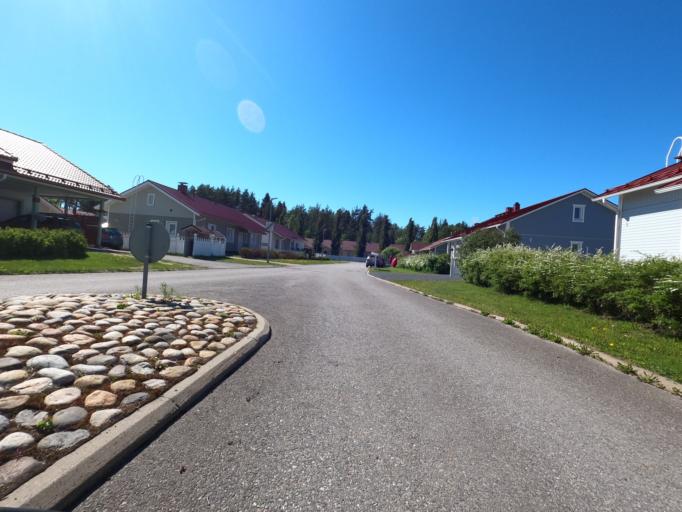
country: FI
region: North Karelia
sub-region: Joensuu
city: Joensuu
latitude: 62.5778
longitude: 29.7723
